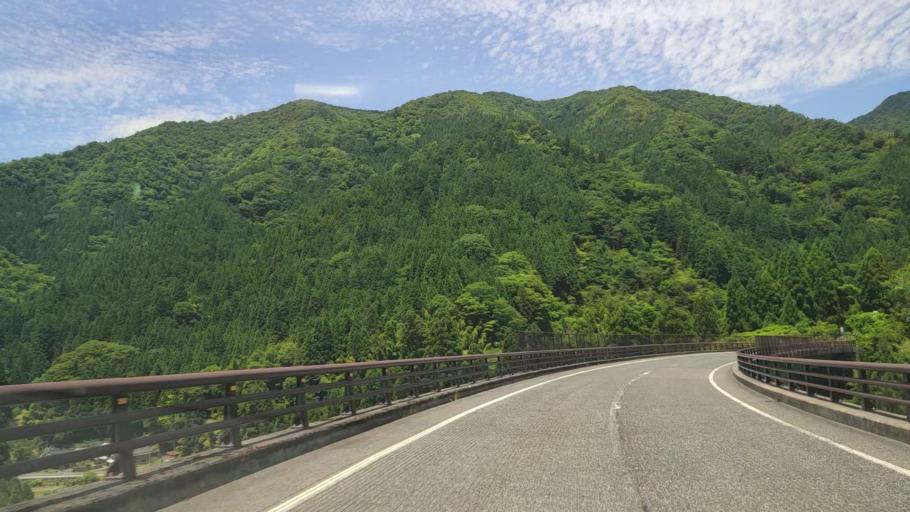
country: JP
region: Tottori
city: Tottori
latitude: 35.3461
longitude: 134.4510
